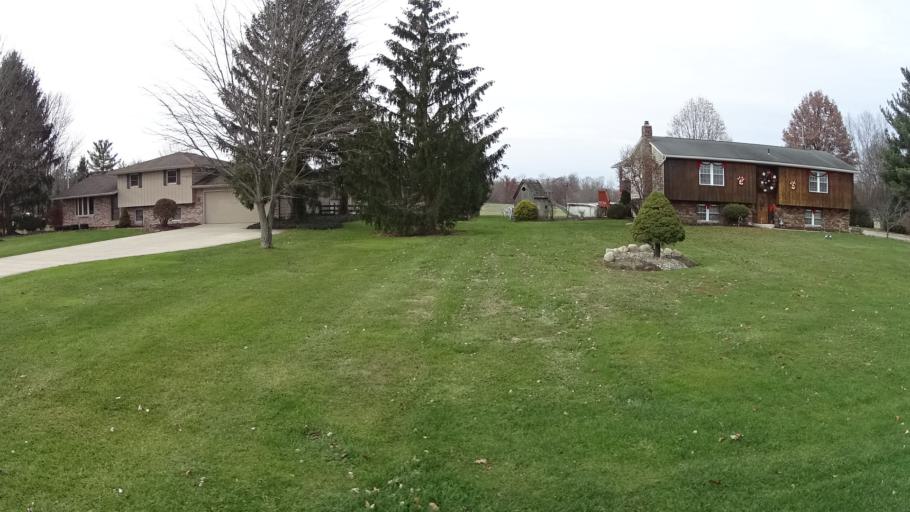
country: US
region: Ohio
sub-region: Lorain County
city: Lagrange
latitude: 41.1843
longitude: -82.0969
